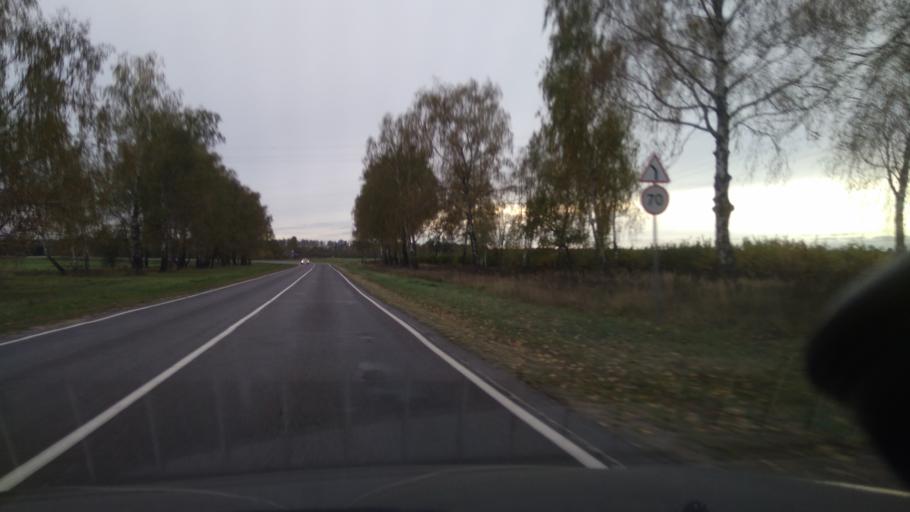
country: BY
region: Minsk
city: Rudzyensk
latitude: 53.6200
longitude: 27.8578
